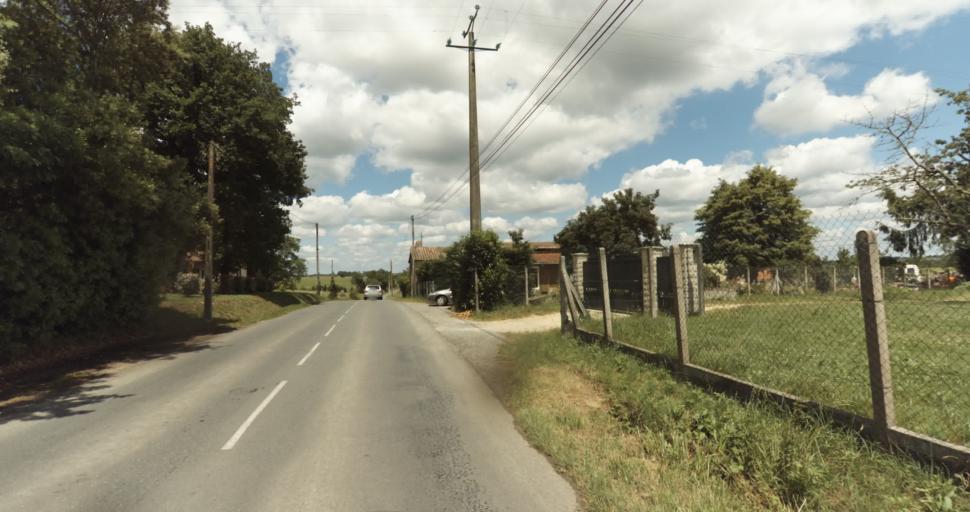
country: FR
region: Aquitaine
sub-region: Departement de la Dordogne
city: Beaumont-du-Perigord
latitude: 44.7329
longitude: 0.7544
